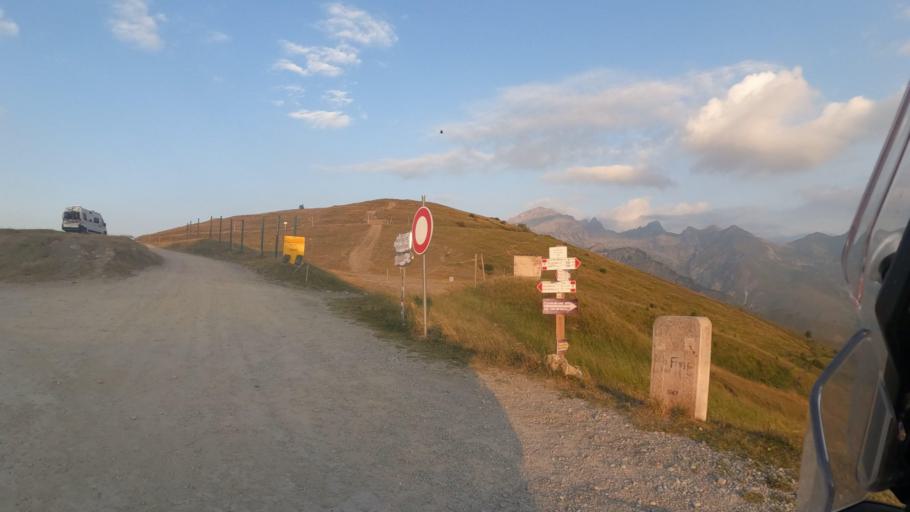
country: IT
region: Piedmont
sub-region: Provincia di Cuneo
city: Limone Piemonte
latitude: 44.1494
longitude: 7.5622
